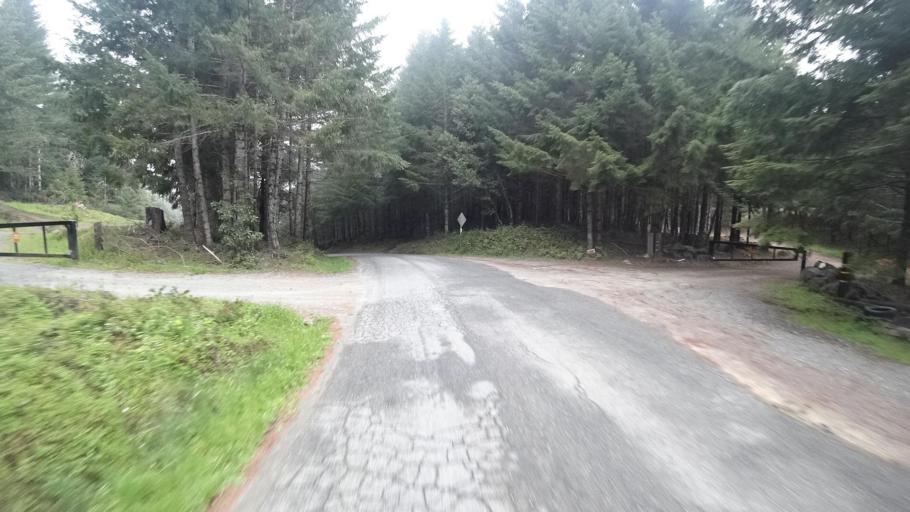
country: US
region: California
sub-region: Humboldt County
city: Redway
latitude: 40.2724
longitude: -123.7681
